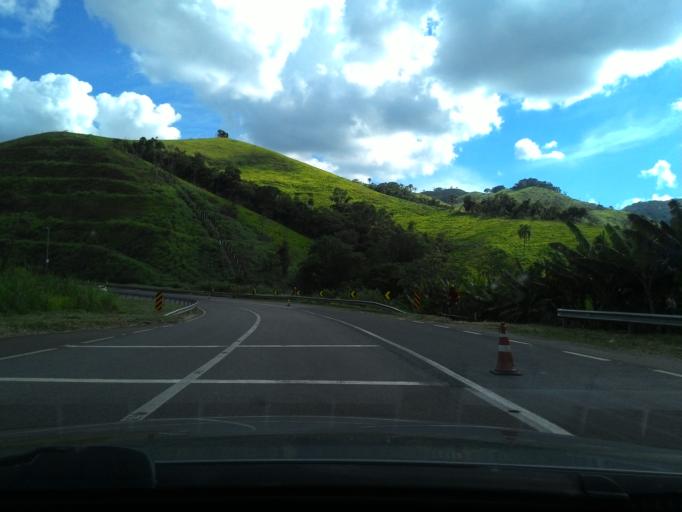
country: BR
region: Sao Paulo
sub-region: Cajati
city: Cajati
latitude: -24.7771
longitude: -48.2110
